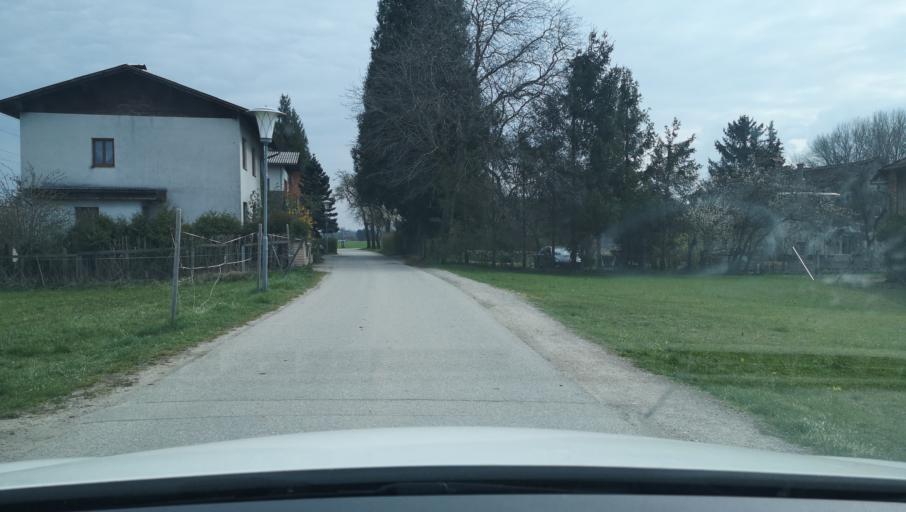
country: AT
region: Lower Austria
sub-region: Politischer Bezirk Amstetten
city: Amstetten
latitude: 48.1127
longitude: 14.8971
